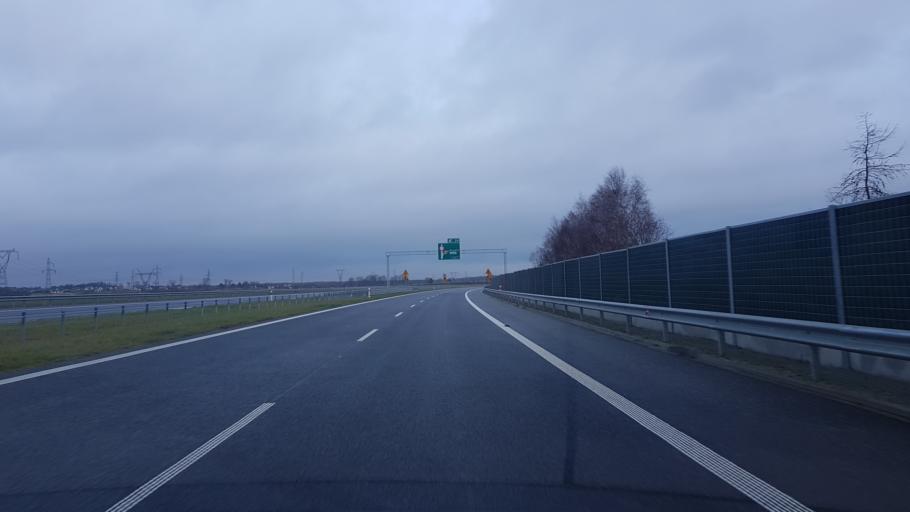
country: PL
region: West Pomeranian Voivodeship
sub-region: Koszalin
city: Koszalin
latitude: 54.2266
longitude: 16.1680
